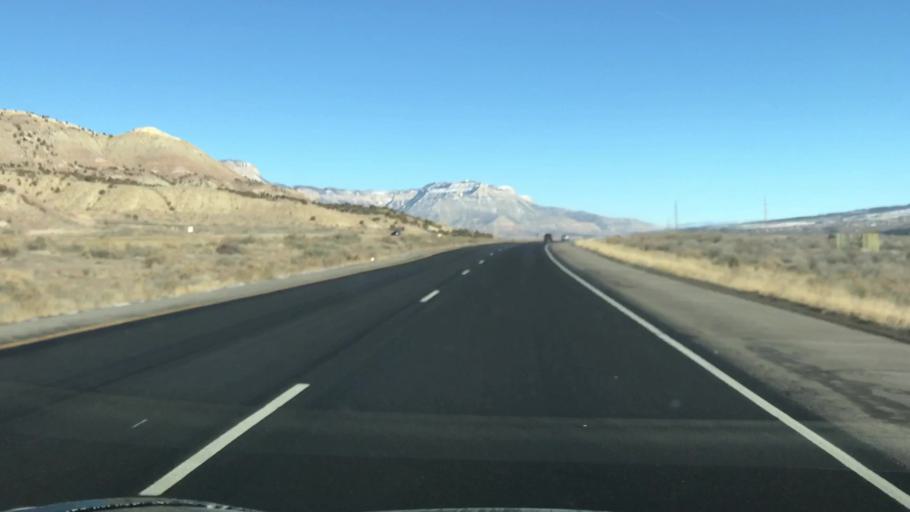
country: US
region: Colorado
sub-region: Garfield County
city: Parachute
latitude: 39.4195
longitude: -108.0882
